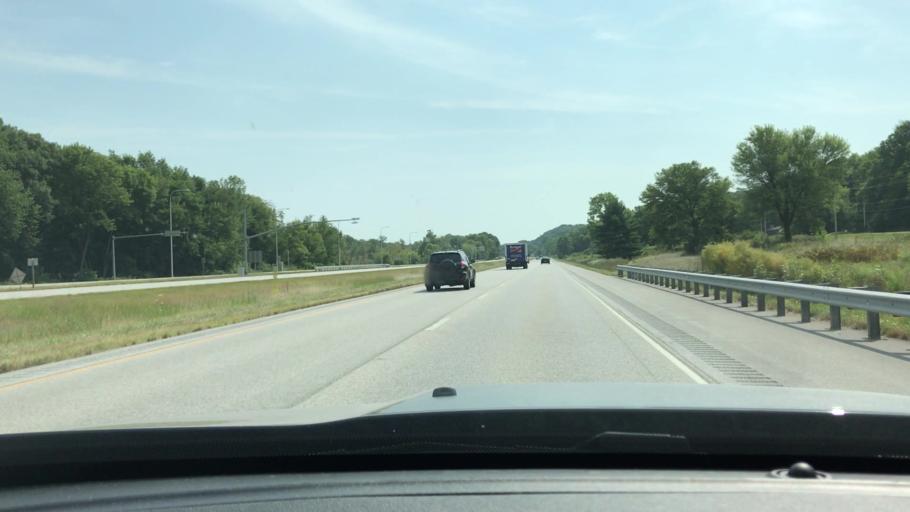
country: US
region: Illinois
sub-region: Rock Island County
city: Coal Valley
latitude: 41.4539
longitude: -90.4322
